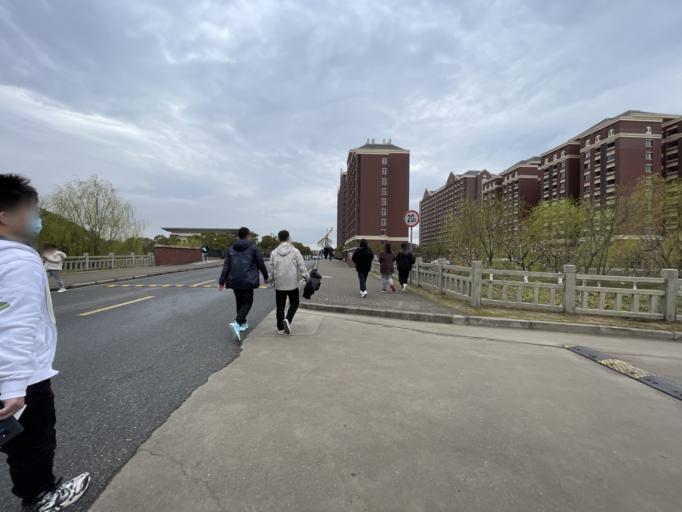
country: CN
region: Shanghai Shi
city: Shuyuan
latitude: 30.8957
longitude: 121.8869
